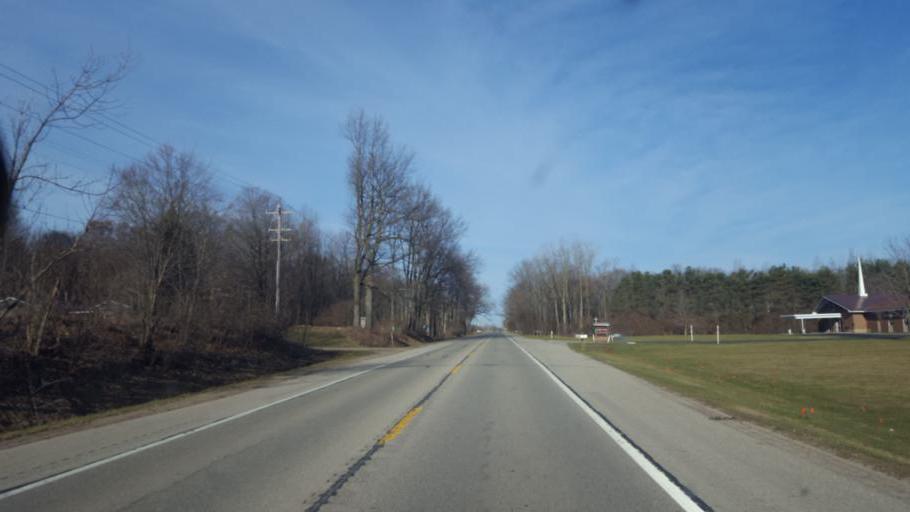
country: US
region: Michigan
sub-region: Montcalm County
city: Edmore
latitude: 43.4080
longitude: -85.0949
